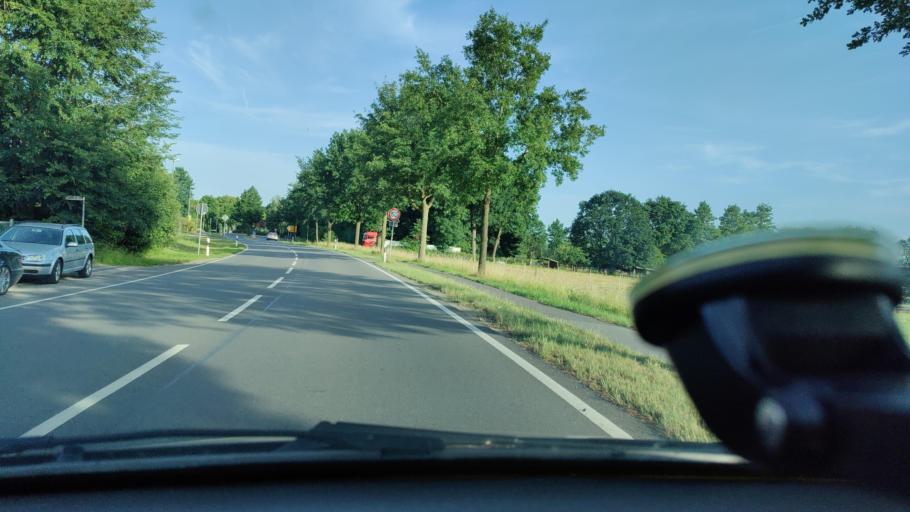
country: DE
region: North Rhine-Westphalia
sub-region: Regierungsbezirk Munster
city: Billerbeck
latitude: 51.9823
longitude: 7.2751
